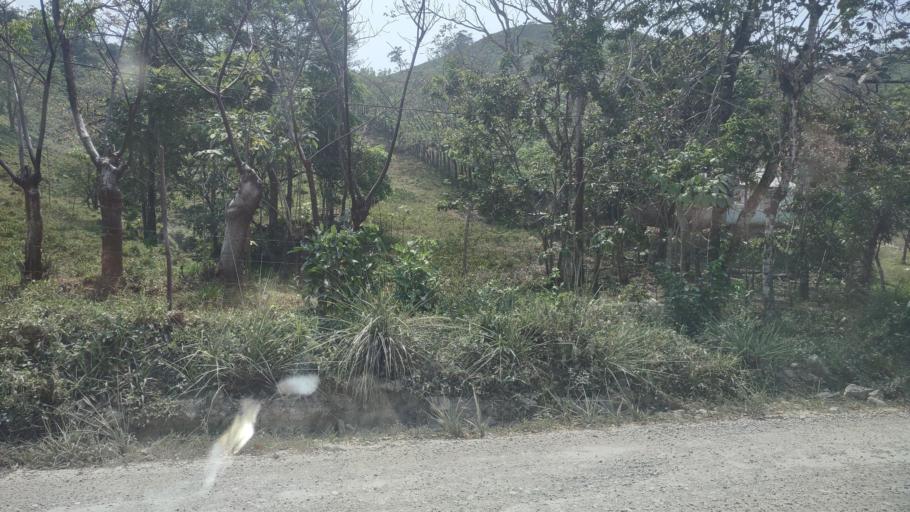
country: MX
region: Tabasco
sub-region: Huimanguillo
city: Francisco Rueda
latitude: 17.5434
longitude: -93.8917
